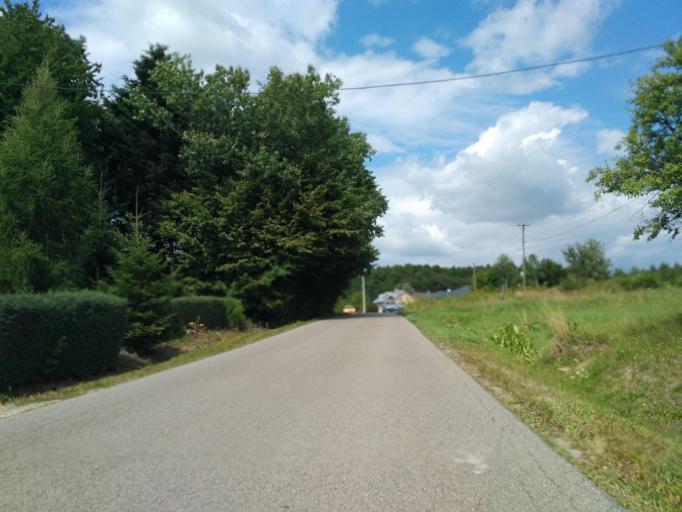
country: PL
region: Subcarpathian Voivodeship
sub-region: Powiat rzeszowski
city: Chmielnik
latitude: 49.9448
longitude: 22.1599
